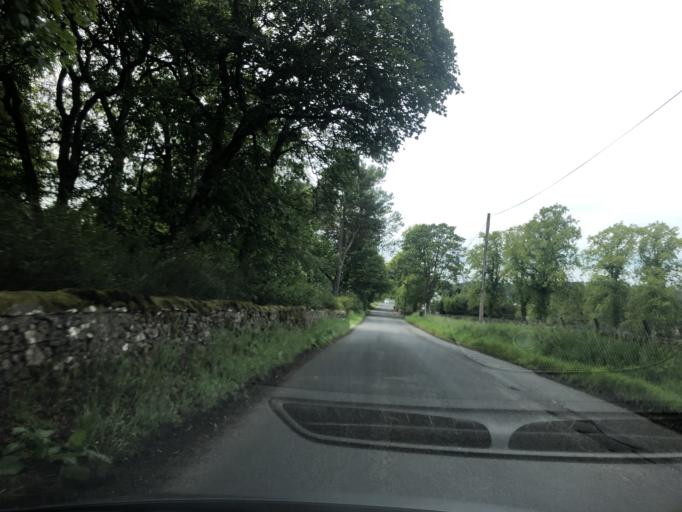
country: GB
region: Scotland
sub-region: The Scottish Borders
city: West Linton
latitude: 55.7433
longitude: -3.3445
